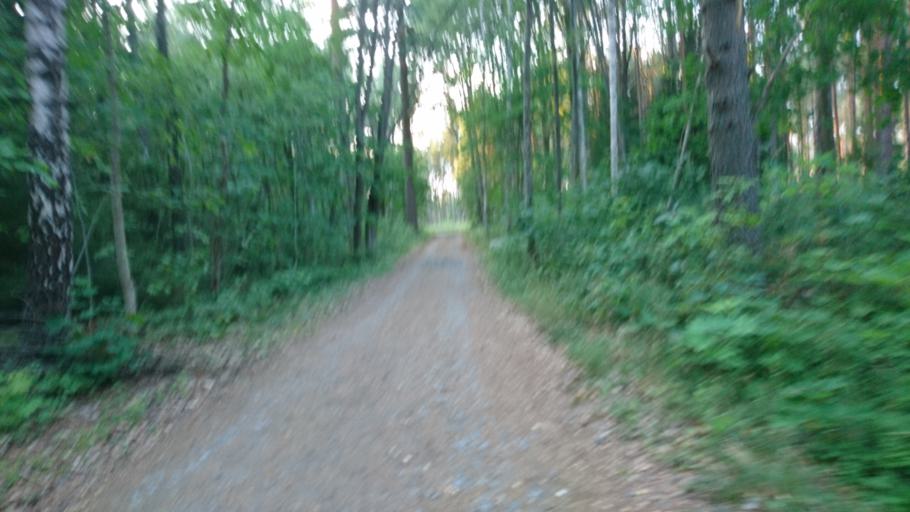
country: SE
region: Uppsala
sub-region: Uppsala Kommun
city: Saevja
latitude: 59.7718
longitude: 17.6514
